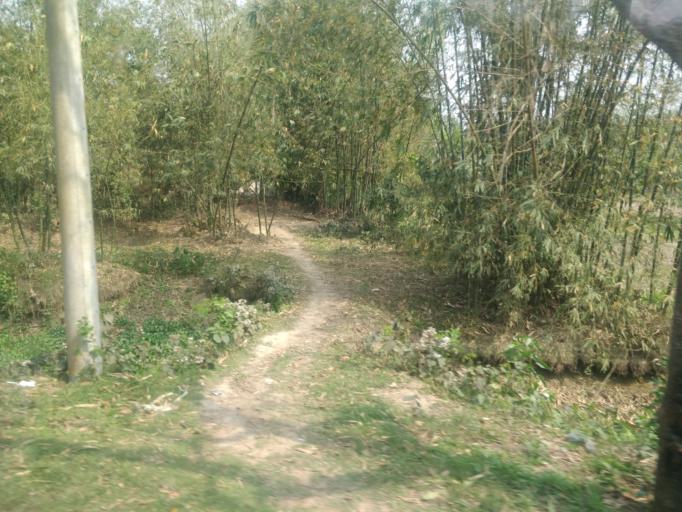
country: BD
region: Sylhet
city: Habiganj
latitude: 24.3115
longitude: 91.4343
